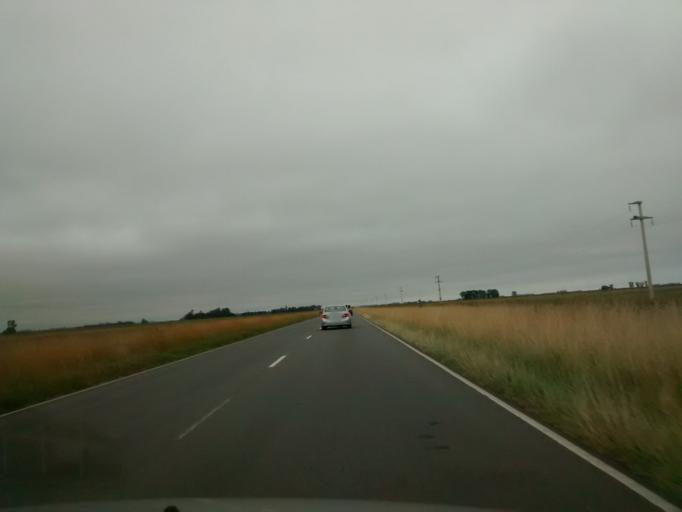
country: AR
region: Buenos Aires
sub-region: Partido de Ayacucho
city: Ayacucho
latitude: -37.0317
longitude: -58.5399
